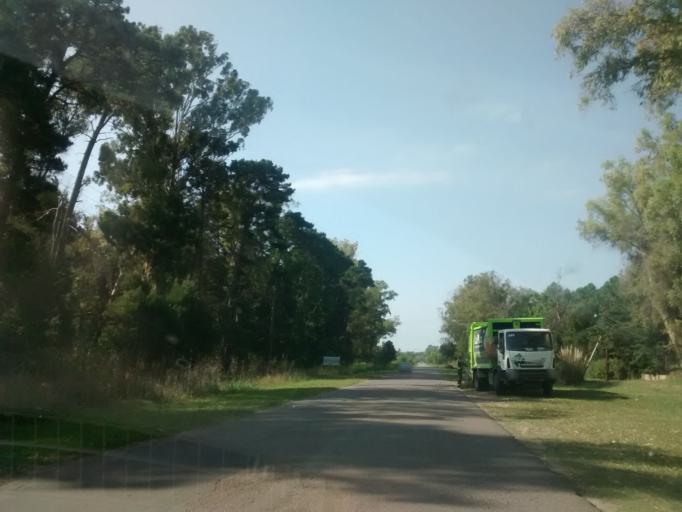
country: AR
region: Buenos Aires
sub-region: Partido de La Plata
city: La Plata
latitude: -34.9870
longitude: -57.8817
